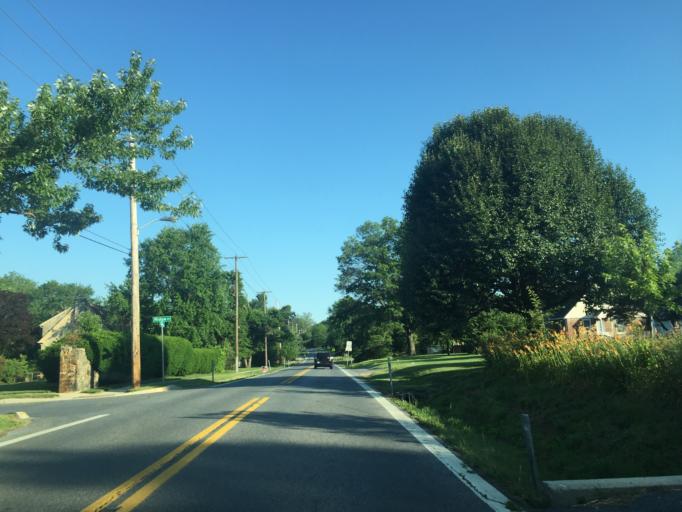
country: US
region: Maryland
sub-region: Baltimore County
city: Catonsville
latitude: 39.2642
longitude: -76.7398
